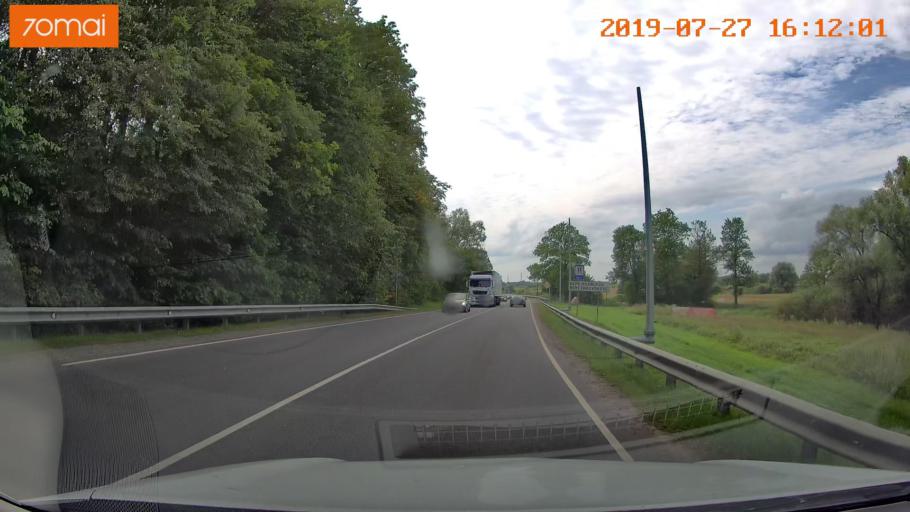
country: RU
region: Kaliningrad
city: Chernyakhovsk
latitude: 54.6312
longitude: 21.6623
